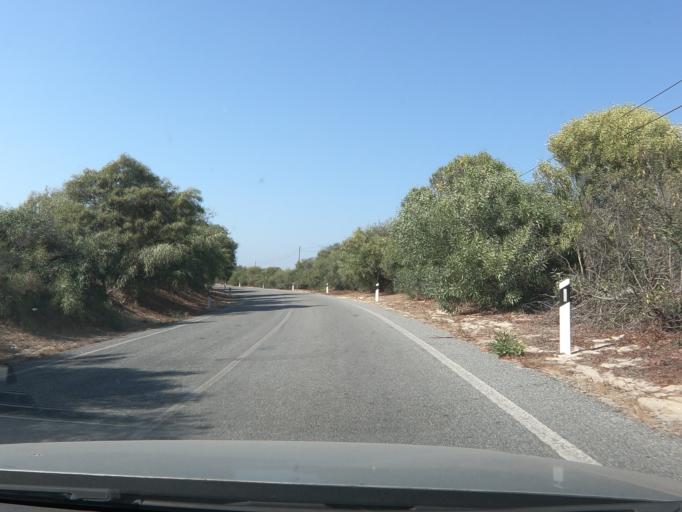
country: PT
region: Setubal
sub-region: Setubal
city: Setubal
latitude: 38.3896
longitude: -8.8004
